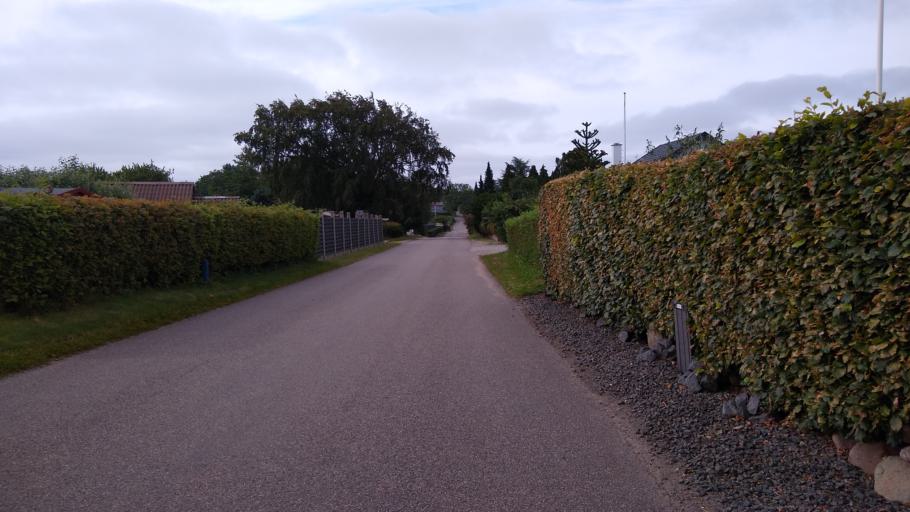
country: DK
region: South Denmark
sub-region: Vejle Kommune
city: Brejning
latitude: 55.6487
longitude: 9.7401
